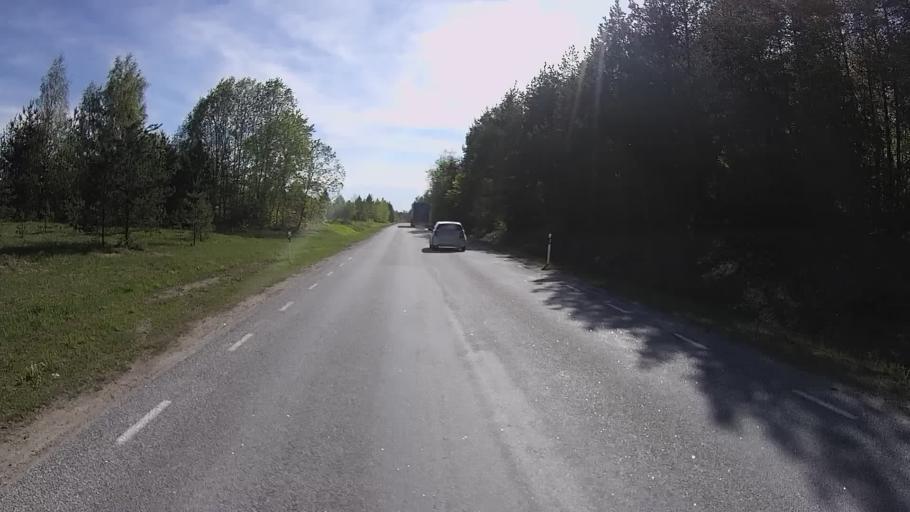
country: EE
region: Vorumaa
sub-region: Antsla vald
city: Vana-Antsla
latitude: 57.9854
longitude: 26.4773
